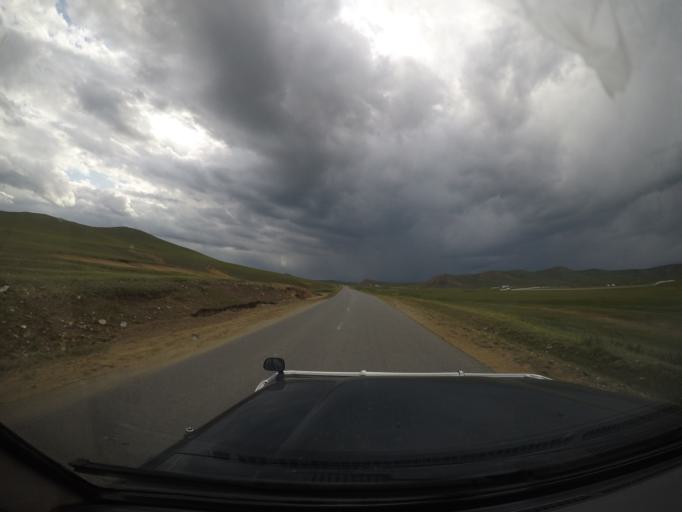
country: MN
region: Central Aimak
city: Bayandelger
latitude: 47.6935
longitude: 108.4941
